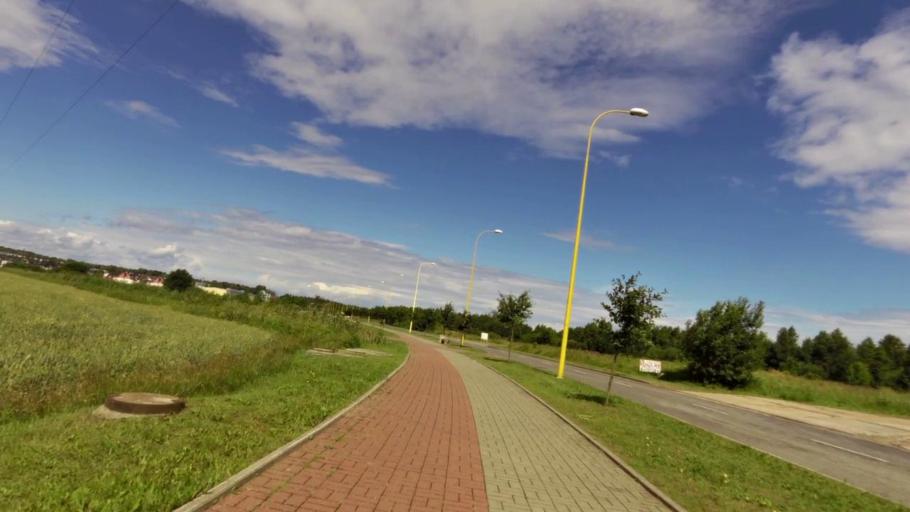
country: PL
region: West Pomeranian Voivodeship
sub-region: Powiat slawienski
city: Darlowo
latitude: 54.4424
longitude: 16.4052
